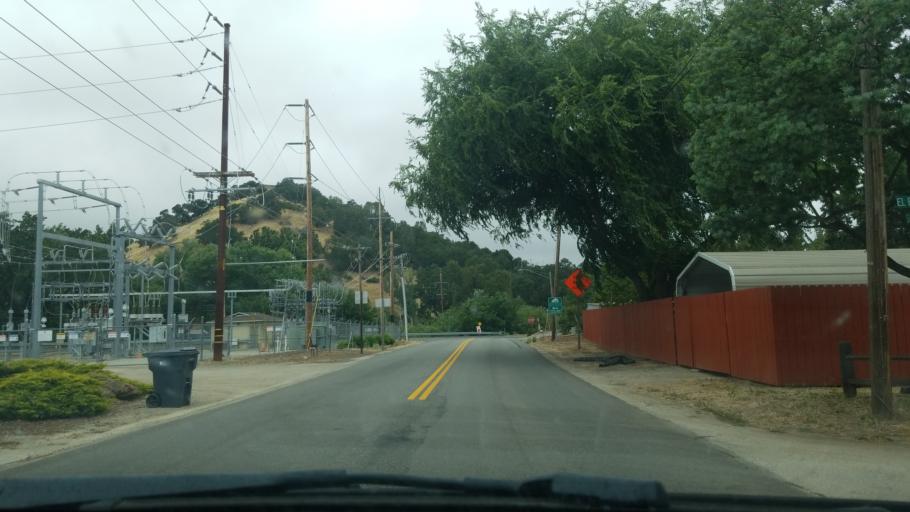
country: US
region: California
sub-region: San Luis Obispo County
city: Atascadero
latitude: 35.4654
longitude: -120.6708
